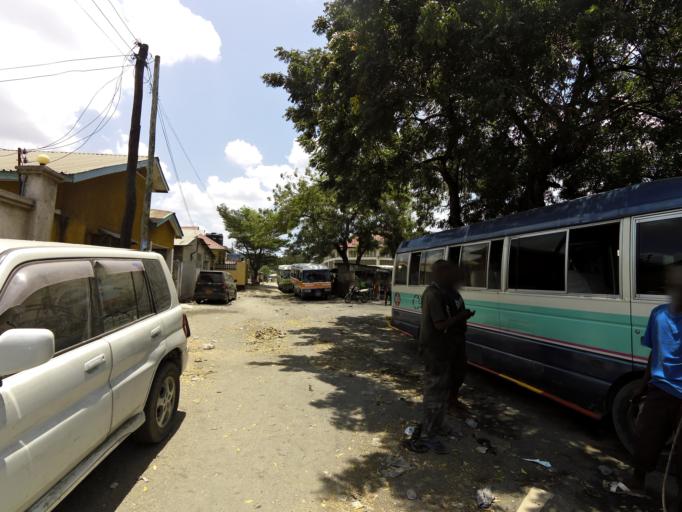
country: TZ
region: Dar es Salaam
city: Dar es Salaam
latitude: -6.8273
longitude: 39.2526
